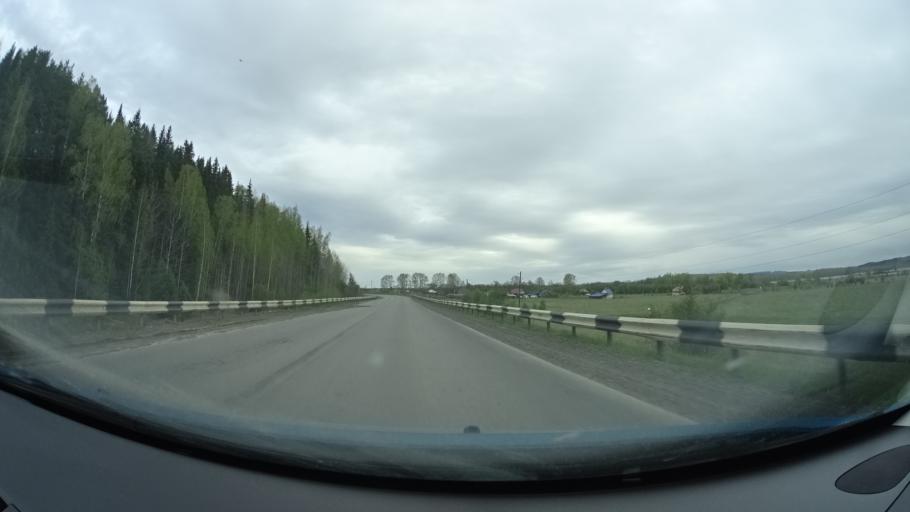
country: RU
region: Perm
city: Osa
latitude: 57.2077
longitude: 55.5890
